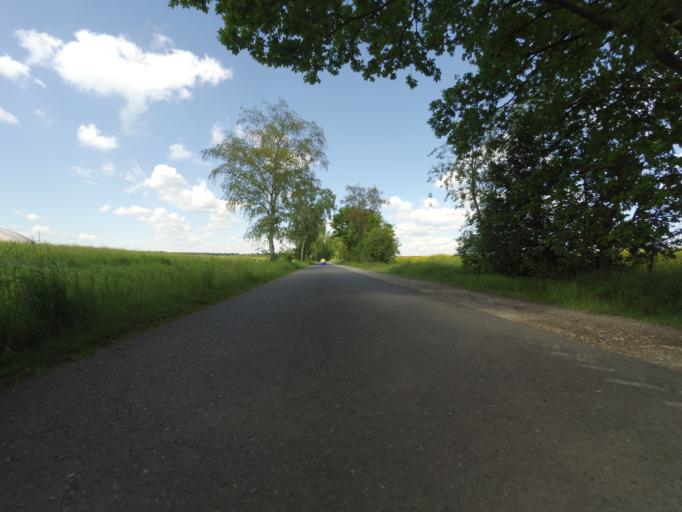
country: DE
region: Lower Saxony
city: Wathlingen
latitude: 52.5312
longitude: 10.1394
